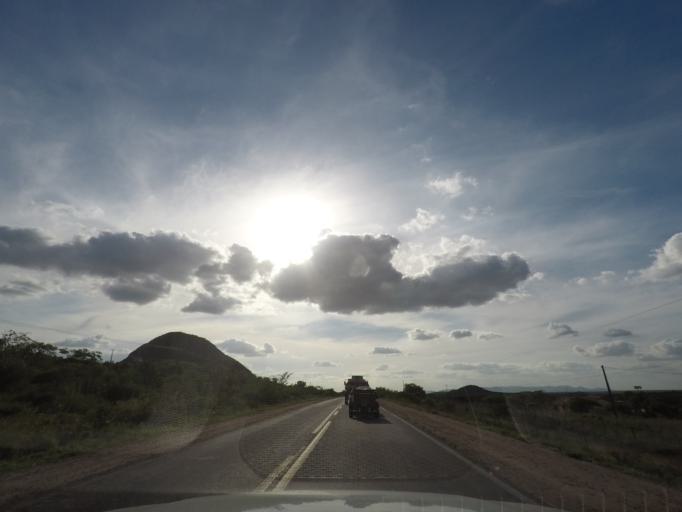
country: BR
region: Bahia
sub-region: Anguera
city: Anguera
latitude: -12.1819
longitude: -39.4593
